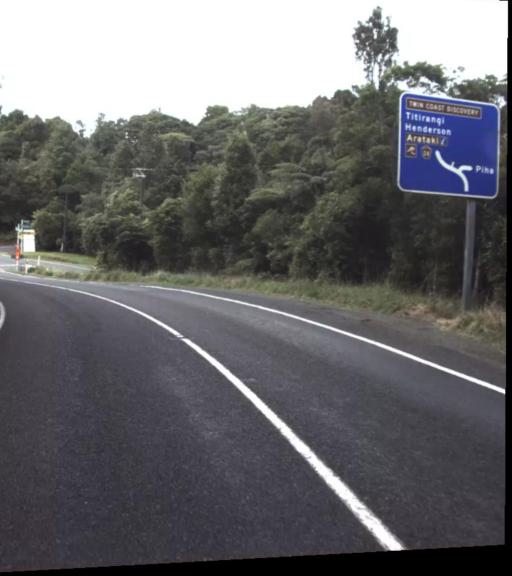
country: NZ
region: Auckland
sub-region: Auckland
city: Titirangi
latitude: -36.9331
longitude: 174.5739
